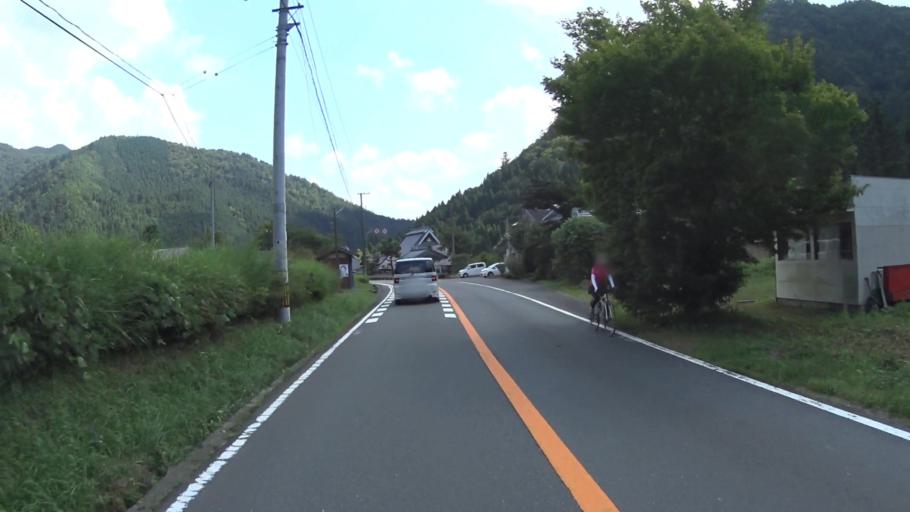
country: JP
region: Kyoto
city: Maizuru
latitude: 35.2972
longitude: 135.5567
